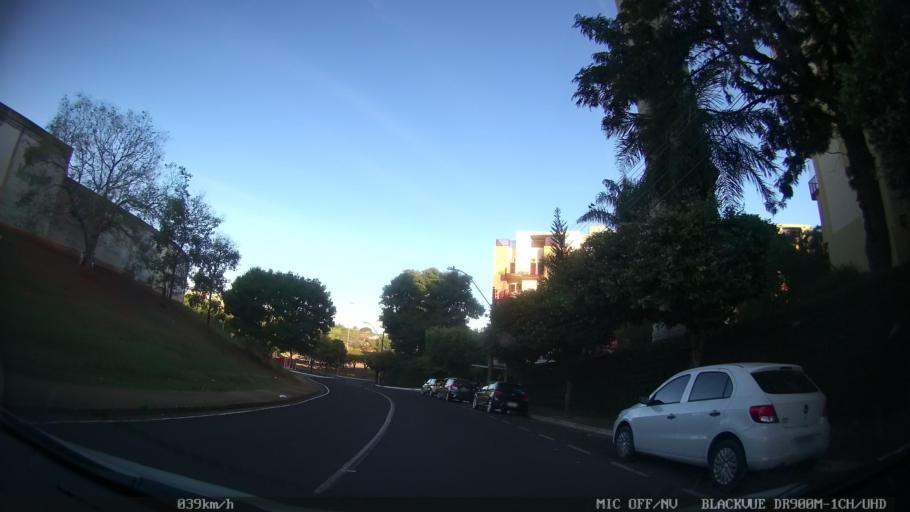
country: BR
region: Sao Paulo
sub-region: Sao Jose Do Rio Preto
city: Sao Jose do Rio Preto
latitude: -20.7984
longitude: -49.3596
